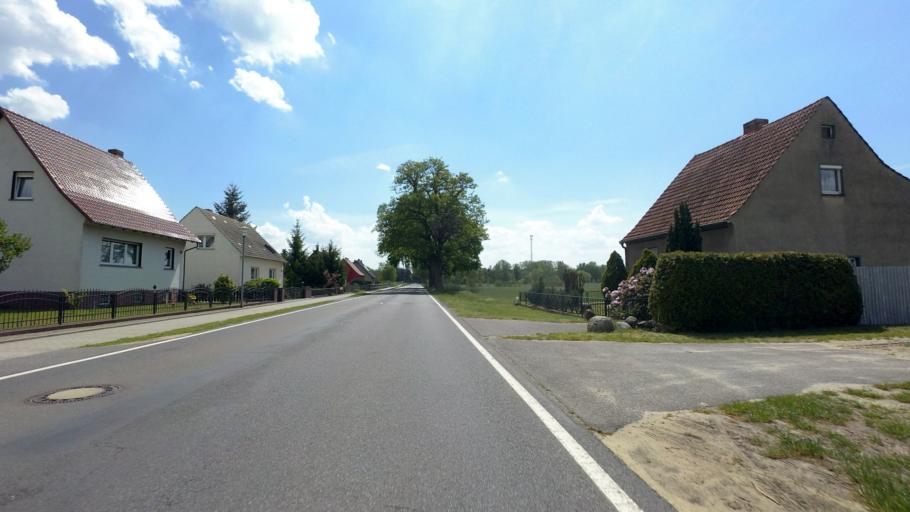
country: DE
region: Brandenburg
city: Neu Zauche
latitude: 51.9239
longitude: 14.0949
